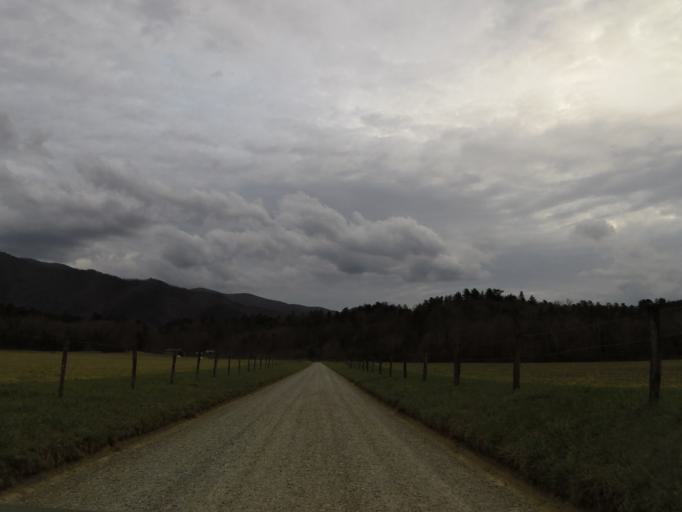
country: US
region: Tennessee
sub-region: Blount County
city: Wildwood
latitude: 35.5914
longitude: -83.8235
